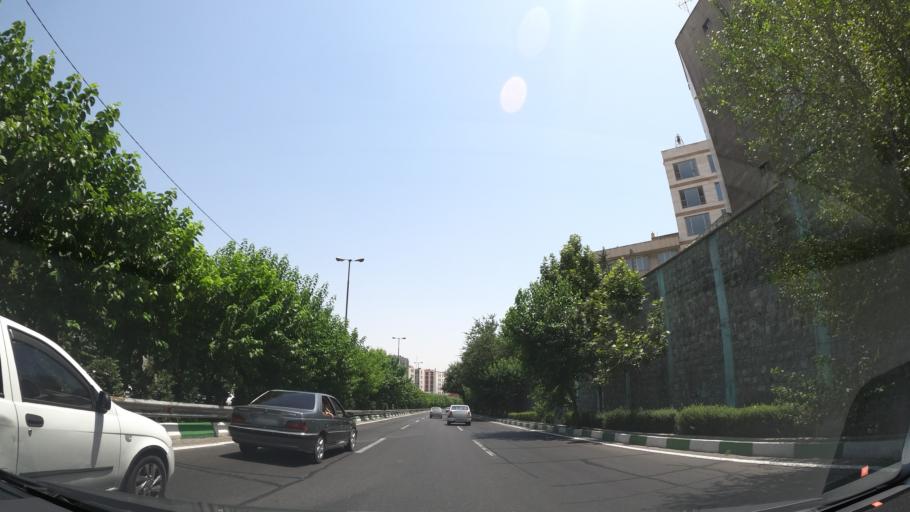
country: IR
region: Tehran
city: Tehran
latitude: 35.7281
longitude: 51.4225
